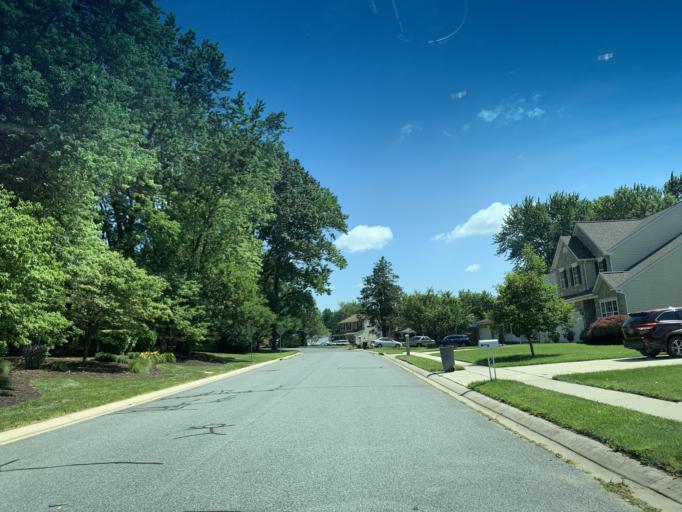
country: US
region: Maryland
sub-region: Harford County
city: South Bel Air
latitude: 39.5192
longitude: -76.3423
